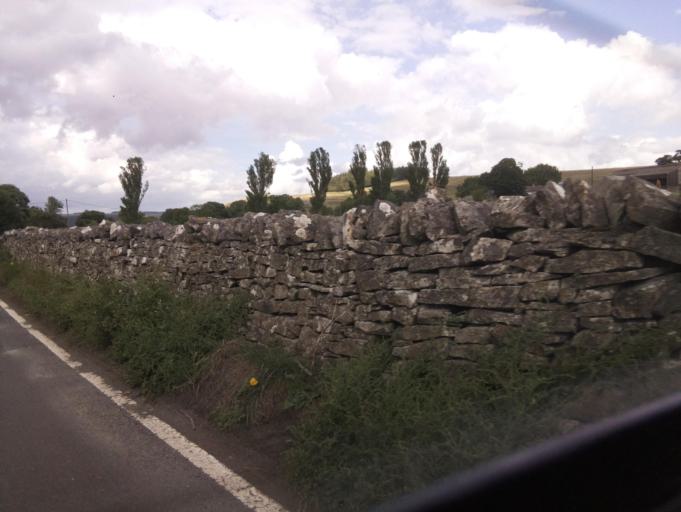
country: GB
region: England
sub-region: North Yorkshire
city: Leyburn
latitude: 54.3738
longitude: -1.8296
